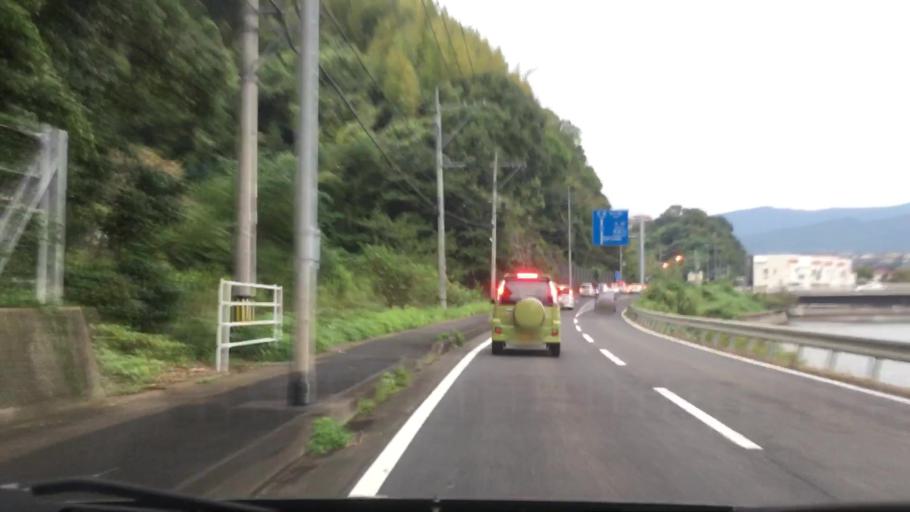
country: JP
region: Nagasaki
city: Sasebo
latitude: 33.1252
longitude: 129.7925
